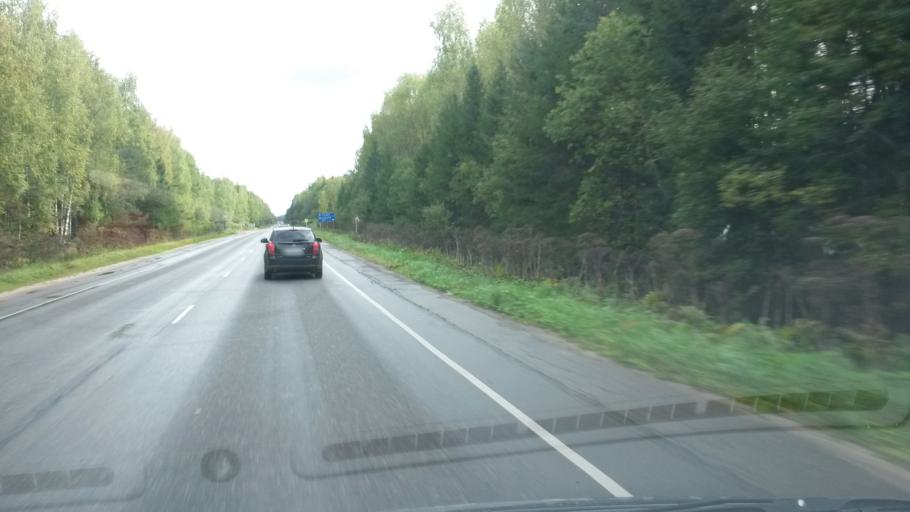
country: RU
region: Ivanovo
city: Kaminskiy
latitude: 57.0475
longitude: 41.3587
